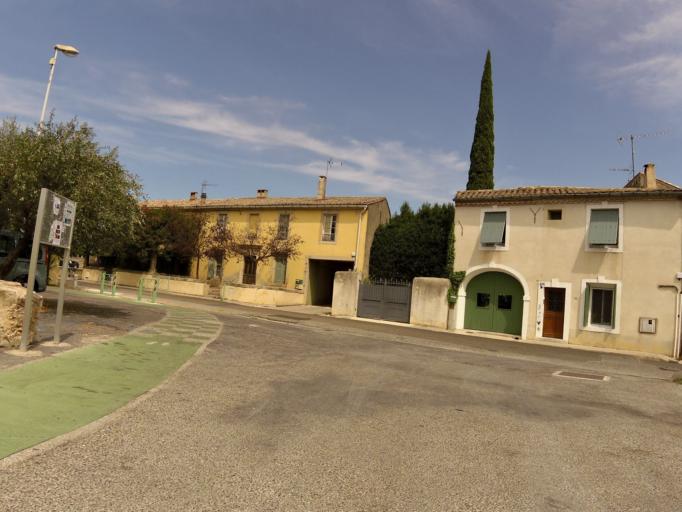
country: FR
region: Languedoc-Roussillon
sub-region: Departement du Gard
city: Congenies
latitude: 43.7777
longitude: 4.1587
